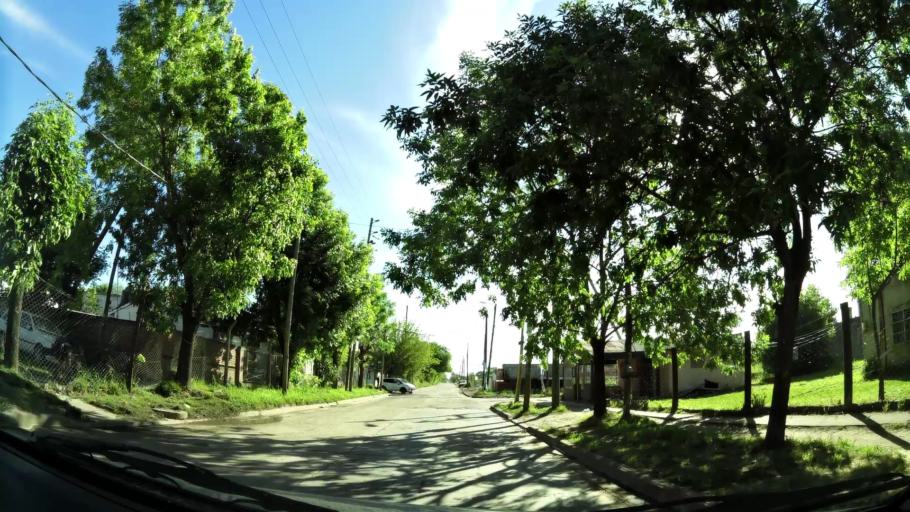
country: AR
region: Buenos Aires
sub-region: Partido de Almirante Brown
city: Adrogue
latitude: -34.8270
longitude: -58.3531
